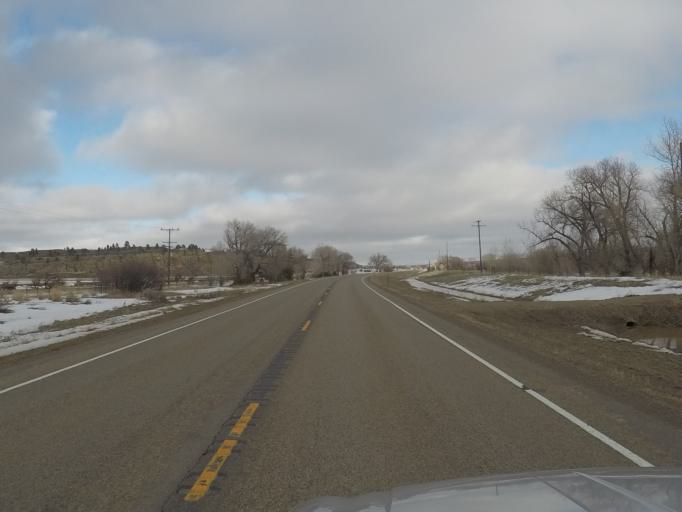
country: US
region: Montana
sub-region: Golden Valley County
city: Ryegate
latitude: 46.2988
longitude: -109.2952
